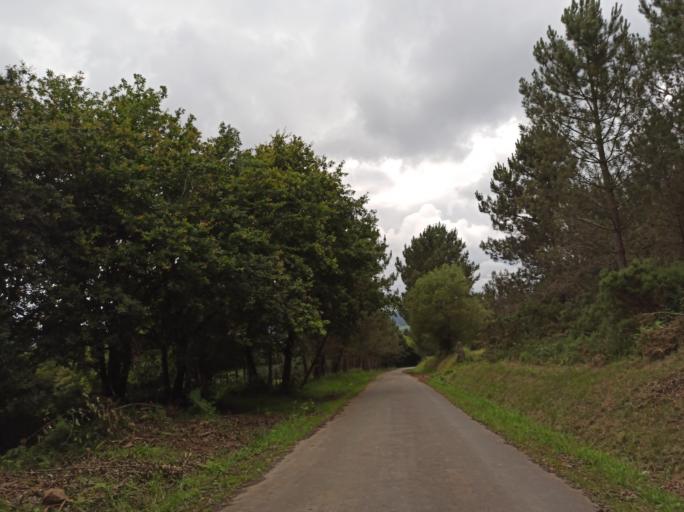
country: ES
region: Galicia
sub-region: Provincia de Pontevedra
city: Silleda
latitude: 42.7712
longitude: -8.1641
